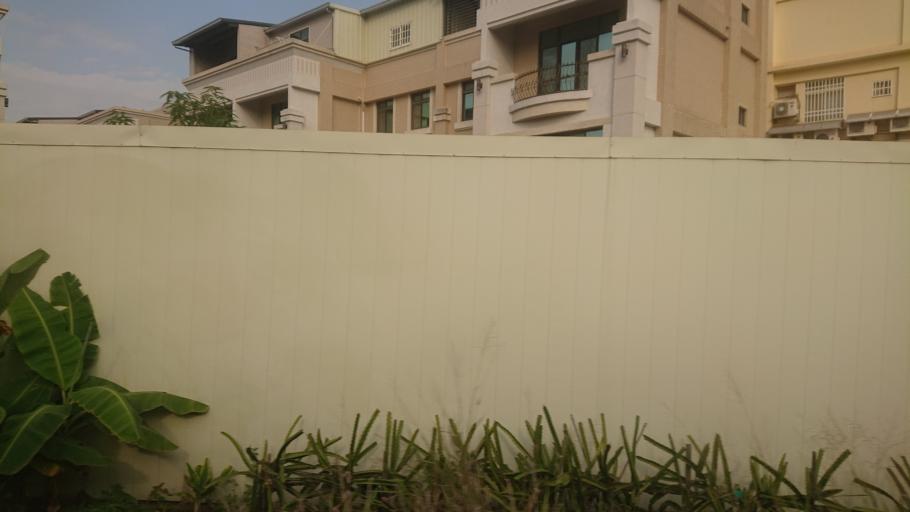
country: TW
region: Taiwan
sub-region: Yunlin
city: Douliu
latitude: 23.7045
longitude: 120.5311
